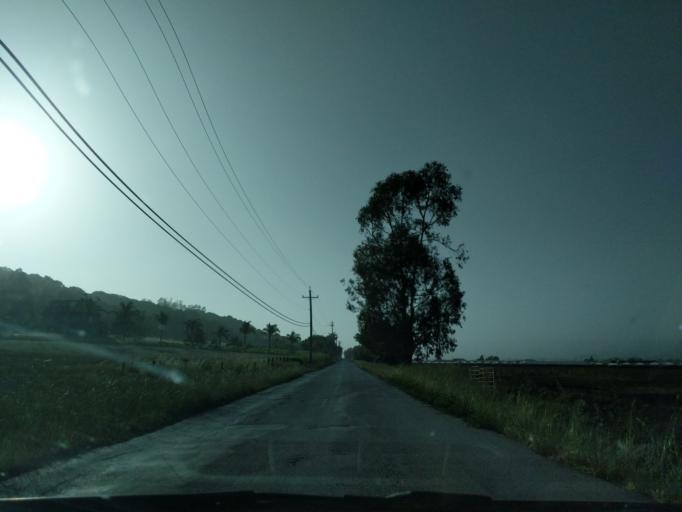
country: US
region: California
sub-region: San Benito County
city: Aromas
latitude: 36.8870
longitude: -121.6851
